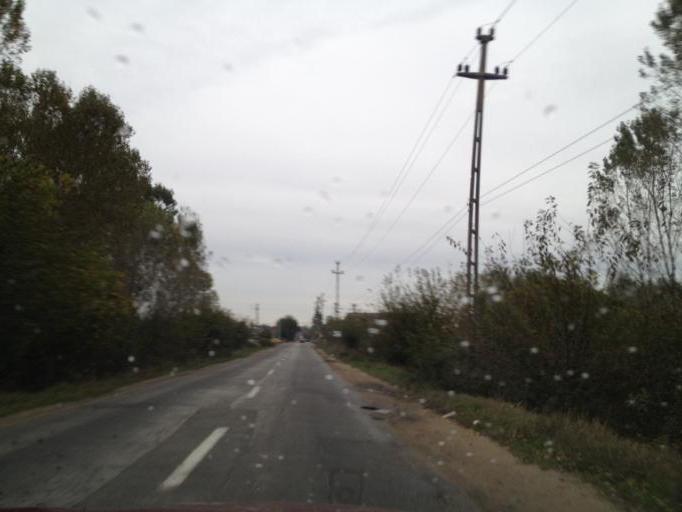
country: RO
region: Dolj
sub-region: Comuna Bucovat
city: Bucovat
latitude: 44.2985
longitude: 23.7540
